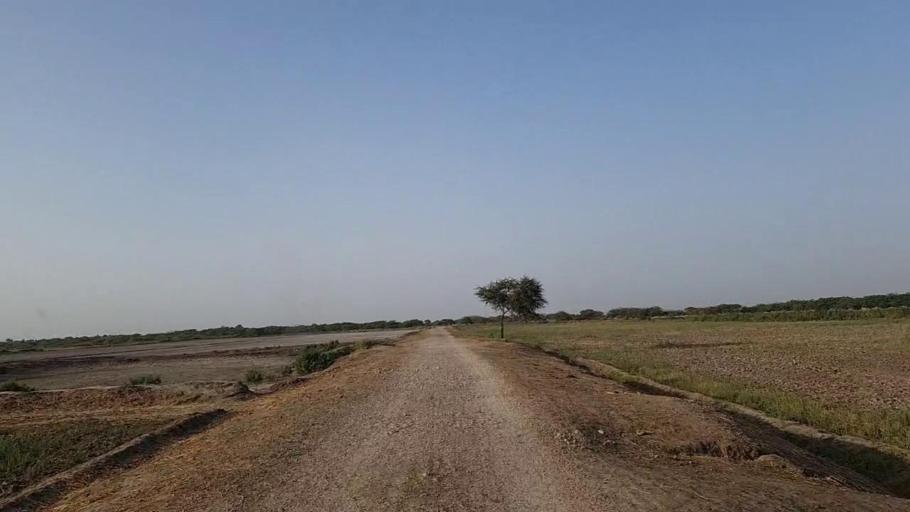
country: PK
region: Sindh
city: Jati
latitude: 24.3801
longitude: 68.1481
